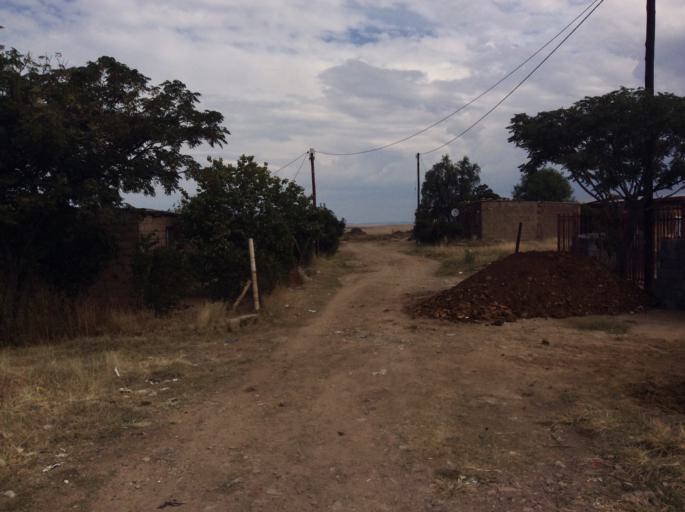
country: LS
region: Mafeteng
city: Mafeteng
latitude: -29.7241
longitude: 27.0319
